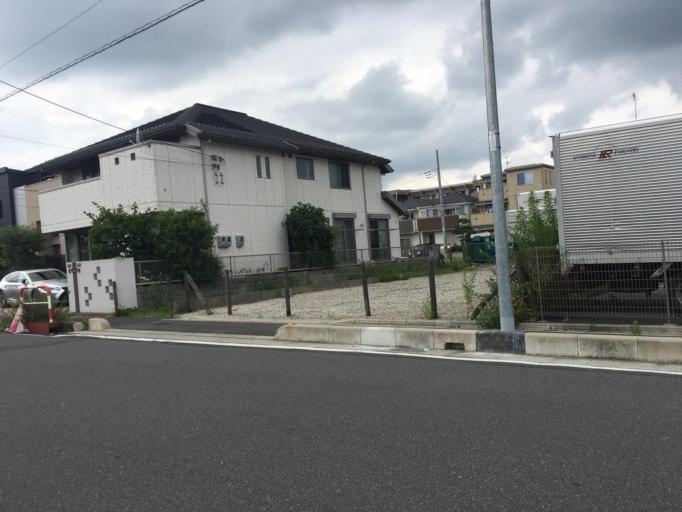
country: JP
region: Saitama
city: Shimotoda
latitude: 35.8186
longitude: 139.6612
